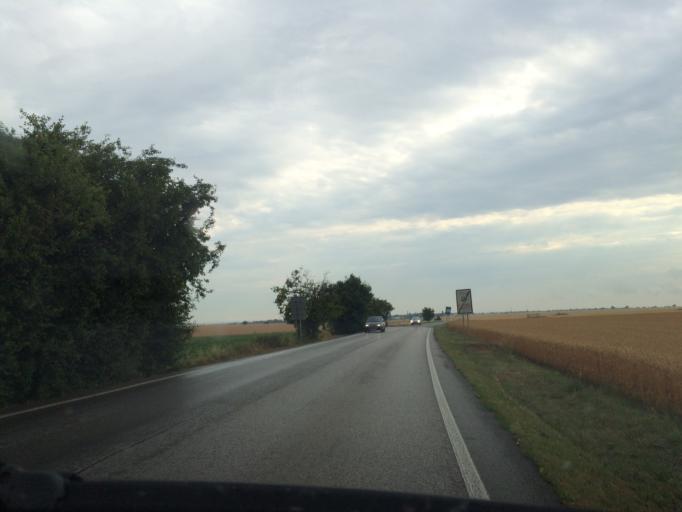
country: CZ
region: Central Bohemia
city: Horomerice
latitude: 50.1181
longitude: 14.3162
